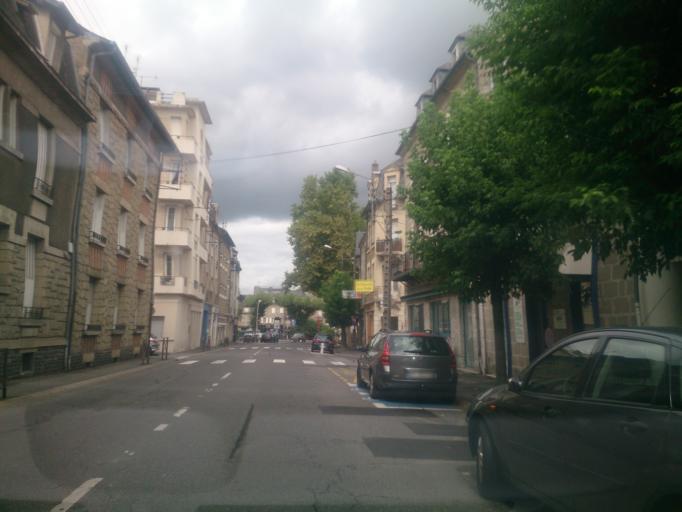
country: FR
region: Limousin
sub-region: Departement de la Correze
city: Brive-la-Gaillarde
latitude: 45.1561
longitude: 1.5367
